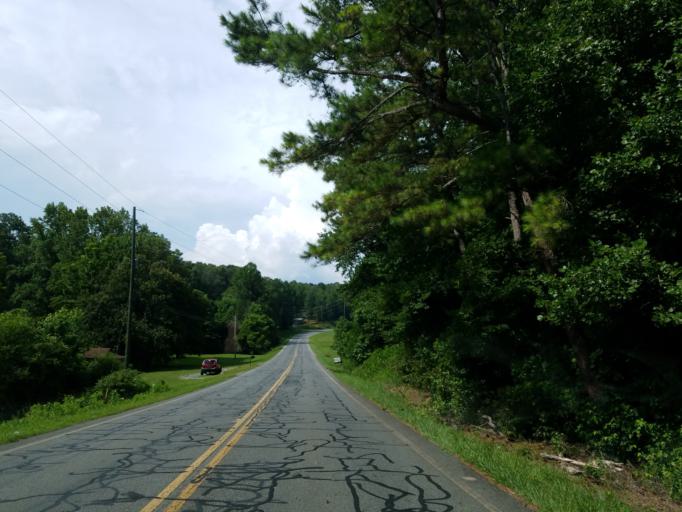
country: US
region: Georgia
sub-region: Gilmer County
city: Ellijay
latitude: 34.6106
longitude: -84.5943
